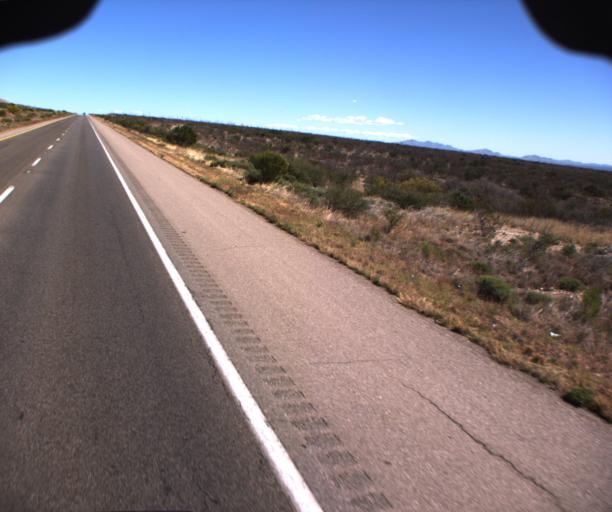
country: US
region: Arizona
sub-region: Cochise County
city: Huachuca City
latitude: 31.7633
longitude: -110.3500
